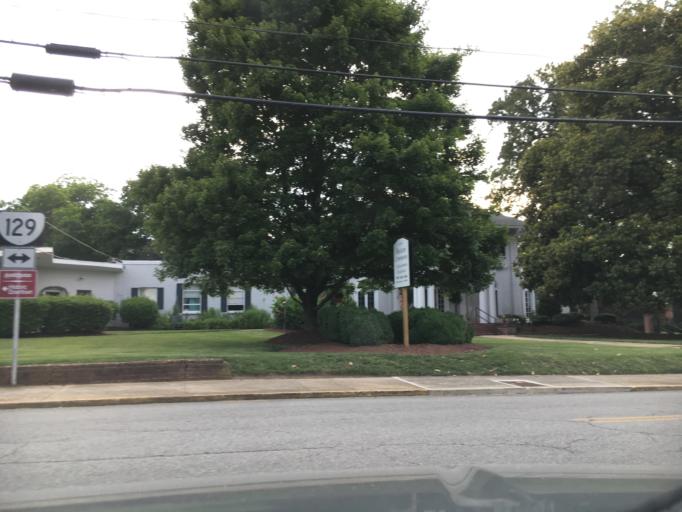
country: US
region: Virginia
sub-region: Halifax County
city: South Boston
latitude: 36.7048
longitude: -78.8986
